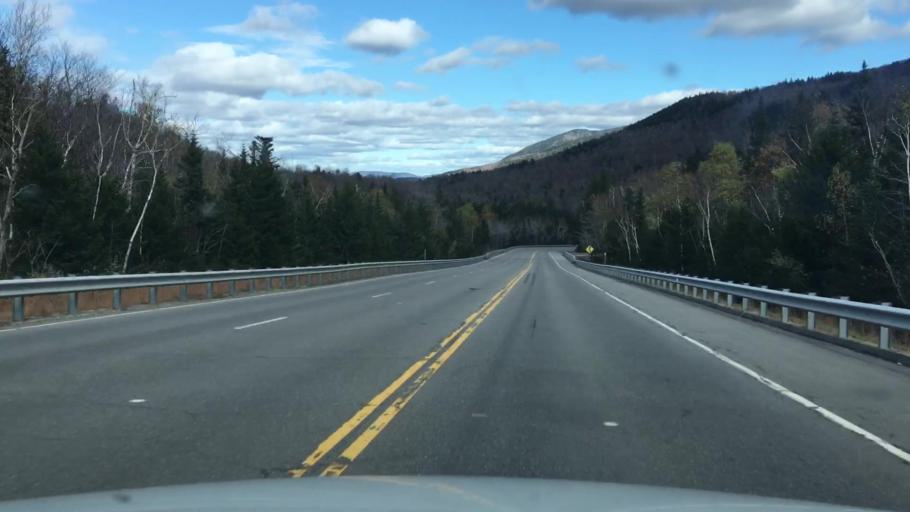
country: US
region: New Hampshire
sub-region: Coos County
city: Gorham
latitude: 44.2700
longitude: -71.2361
